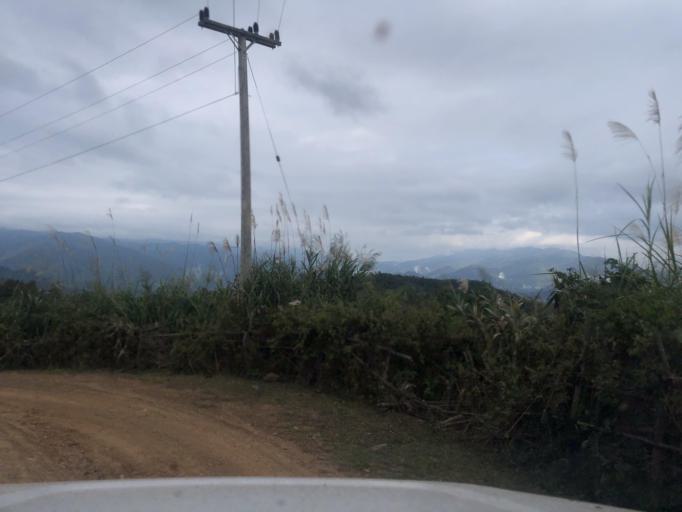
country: LA
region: Phongsali
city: Khoa
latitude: 21.2676
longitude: 102.5854
